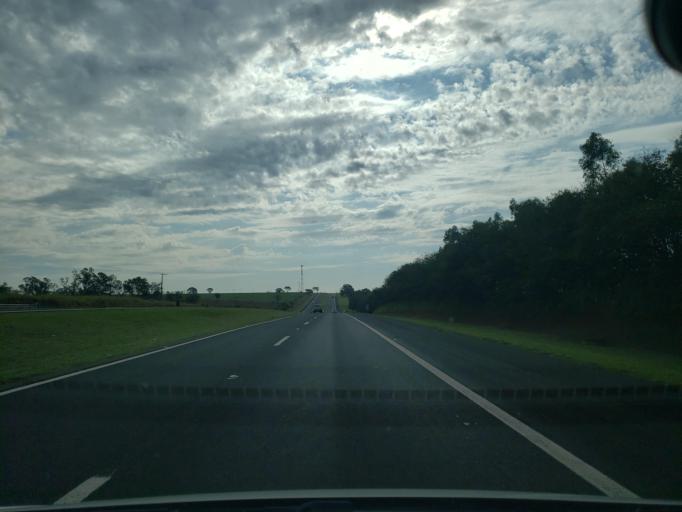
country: BR
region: Sao Paulo
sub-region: Birigui
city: Birigui
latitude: -21.3457
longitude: -50.3179
